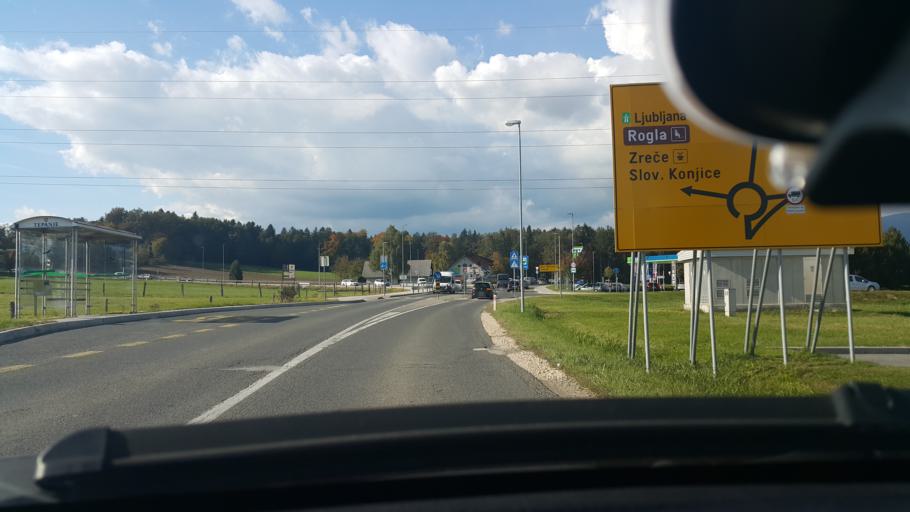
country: SI
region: Slovenska Konjice
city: Slovenske Konjice
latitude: 46.3397
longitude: 15.4703
